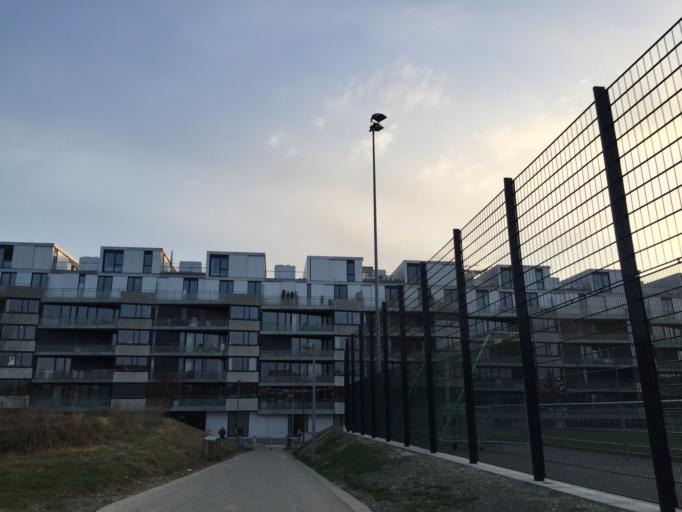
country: CH
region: Bern
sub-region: Bern-Mittelland District
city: Koniz
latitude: 46.9370
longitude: 7.4195
